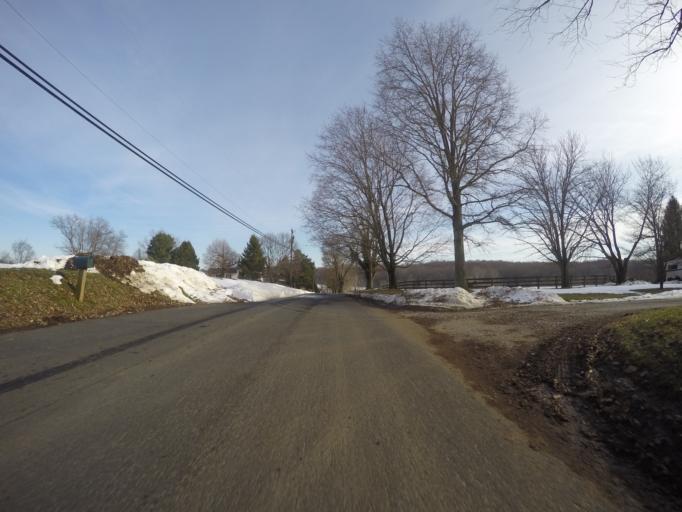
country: US
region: Maryland
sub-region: Baltimore County
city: Hunt Valley
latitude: 39.5516
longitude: -76.5857
